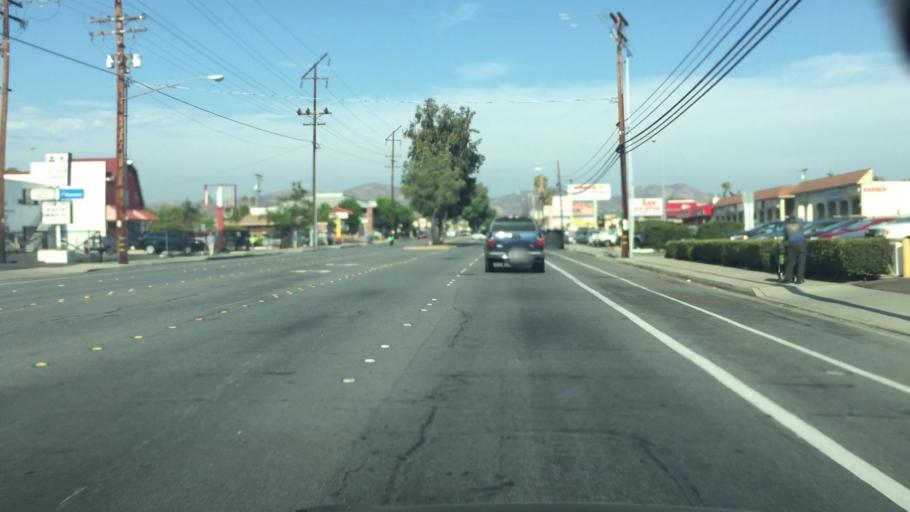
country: US
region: California
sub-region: San Diego County
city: Bostonia
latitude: 32.8076
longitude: -116.9498
